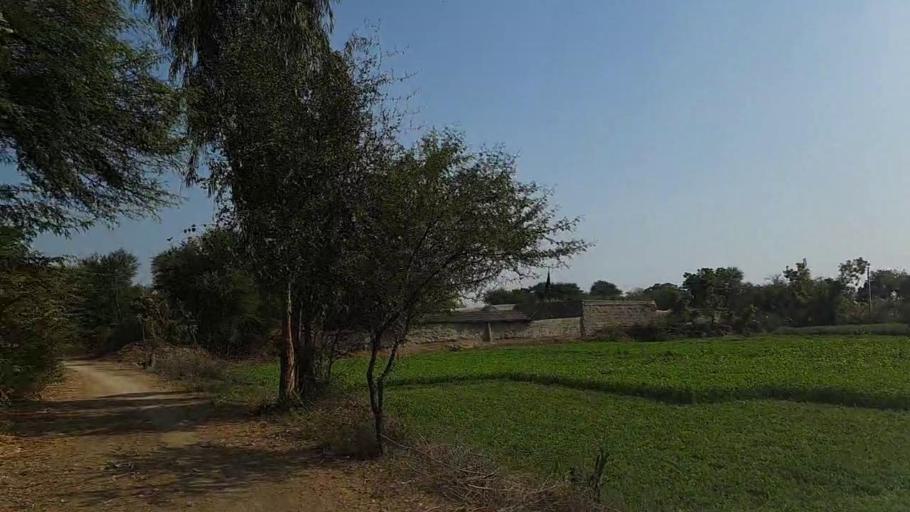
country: PK
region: Sindh
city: Jam Sahib
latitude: 26.2604
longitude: 68.5299
